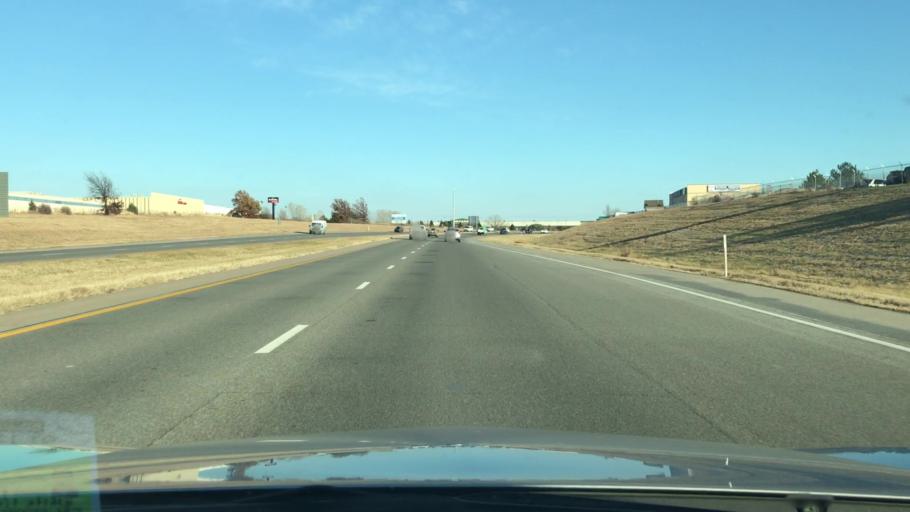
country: US
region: Kansas
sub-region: Sedgwick County
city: Bellaire
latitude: 37.7443
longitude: -97.2389
